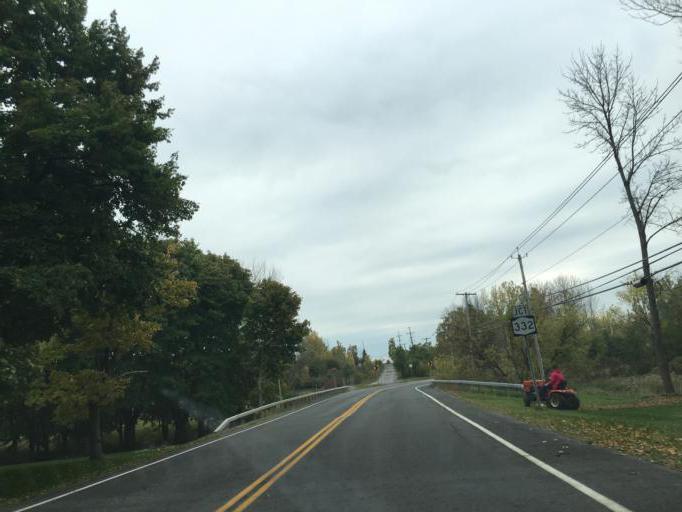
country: US
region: New York
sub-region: Ontario County
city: Canandaigua
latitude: 42.9254
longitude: -77.3079
